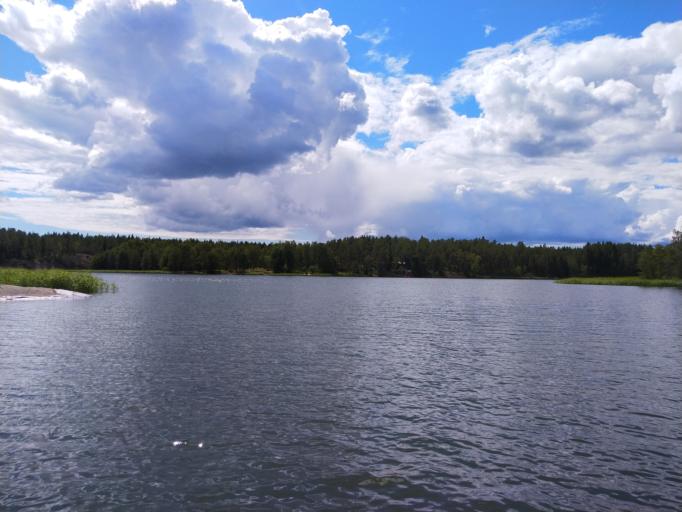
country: FI
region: Uusimaa
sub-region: Raaseporin
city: Karis
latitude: 59.9717
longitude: 23.7043
